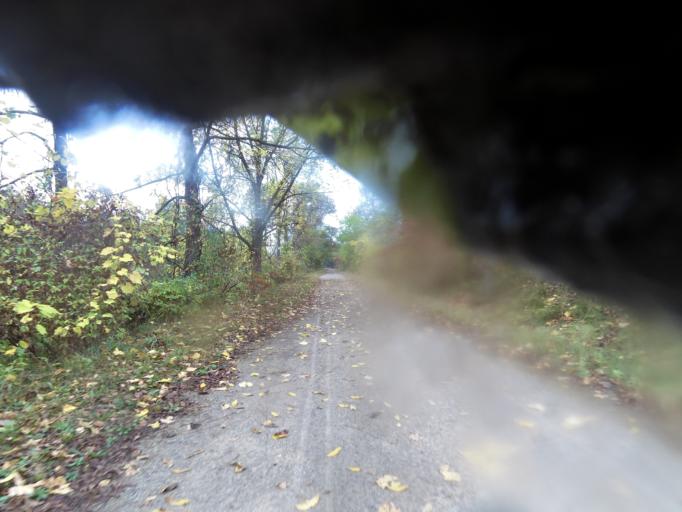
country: CA
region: Ontario
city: Brantford
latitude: 43.1344
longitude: -80.2269
